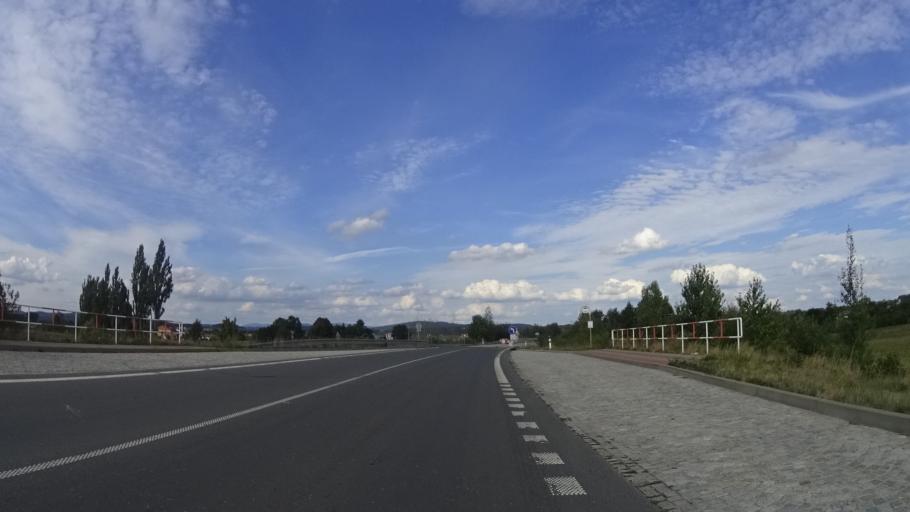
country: CZ
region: Olomoucky
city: Moravicany
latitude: 49.7874
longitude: 16.9627
